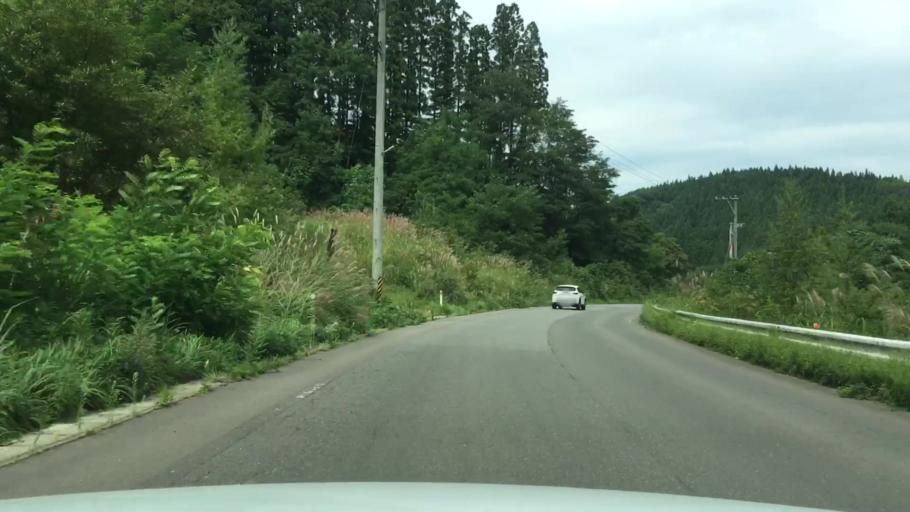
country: JP
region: Aomori
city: Shimokizukuri
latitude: 40.7440
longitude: 140.2416
